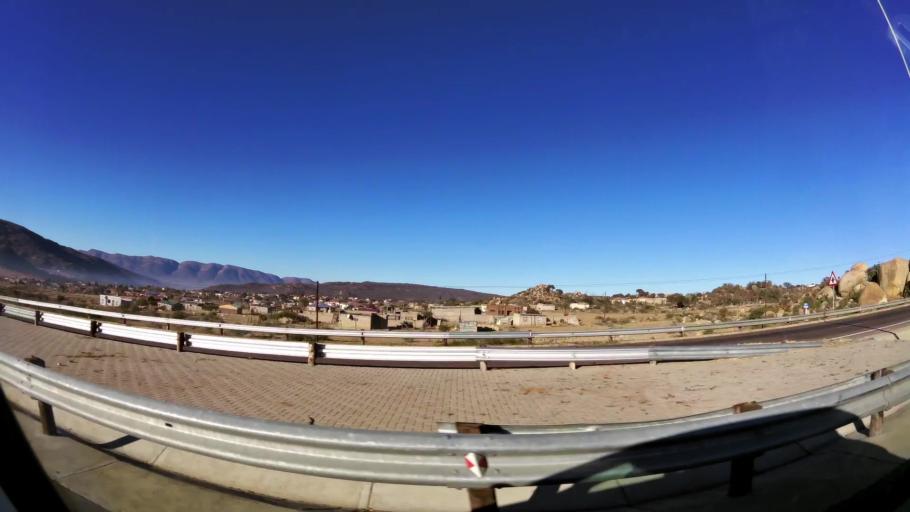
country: ZA
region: Limpopo
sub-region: Capricorn District Municipality
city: Mankoeng
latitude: -23.9136
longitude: 29.7861
